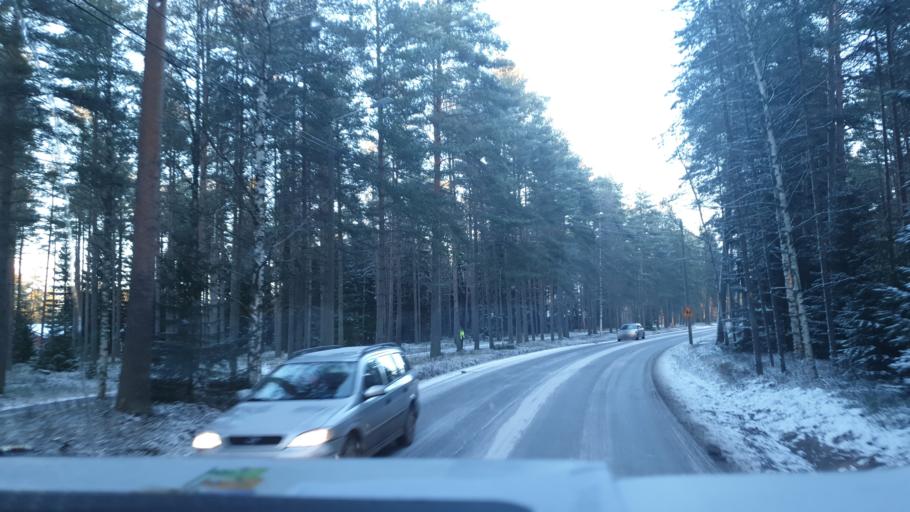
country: FI
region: Central Ostrobothnia
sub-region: Kokkola
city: Kokkola
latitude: 63.8198
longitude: 23.0760
